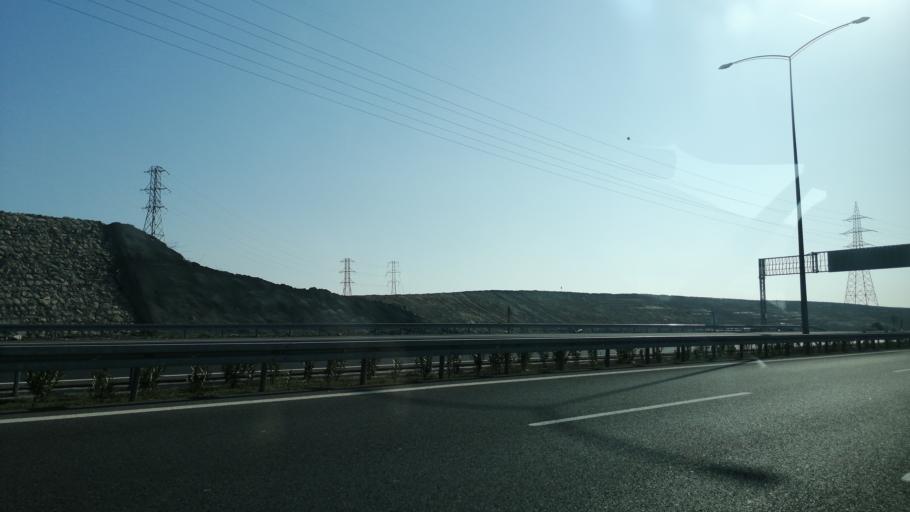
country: TR
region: Kocaeli
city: Tavsanli
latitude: 40.7925
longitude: 29.5125
